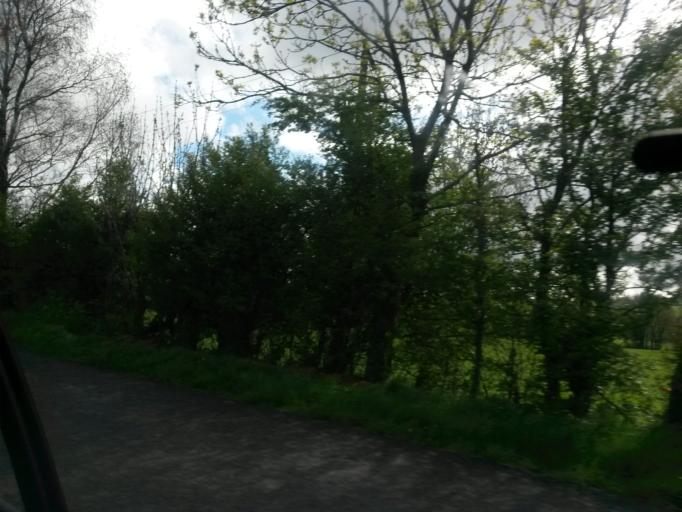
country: IE
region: Leinster
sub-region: Loch Garman
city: Ferns
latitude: 52.5748
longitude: -6.5169
